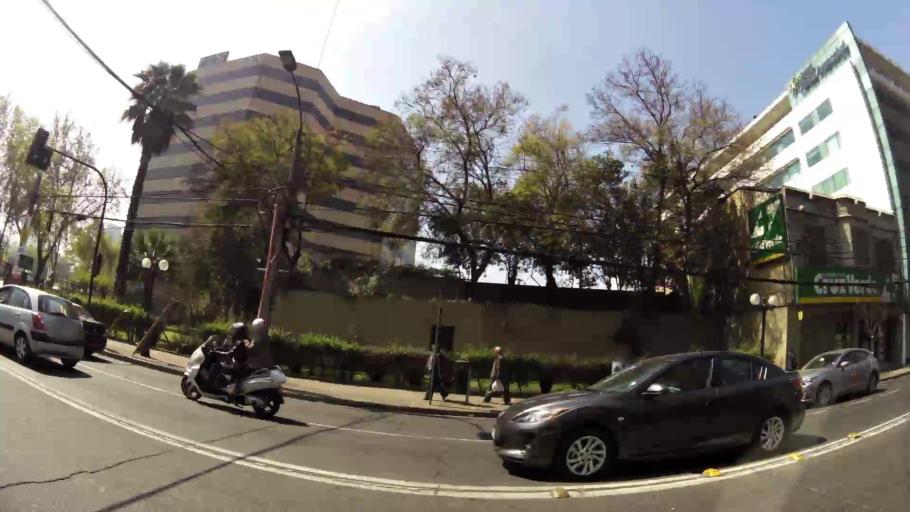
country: CL
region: Santiago Metropolitan
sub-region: Provincia de Santiago
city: Santiago
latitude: -33.4341
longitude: -70.6264
